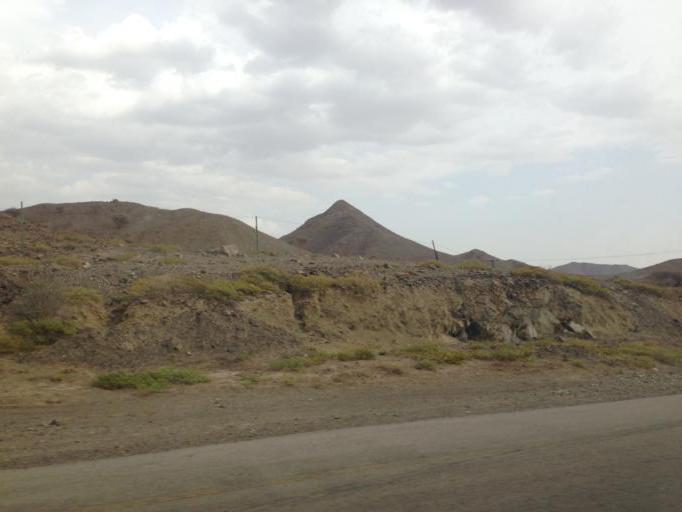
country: OM
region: Ash Sharqiyah
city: Badiyah
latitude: 22.5504
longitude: 59.0006
